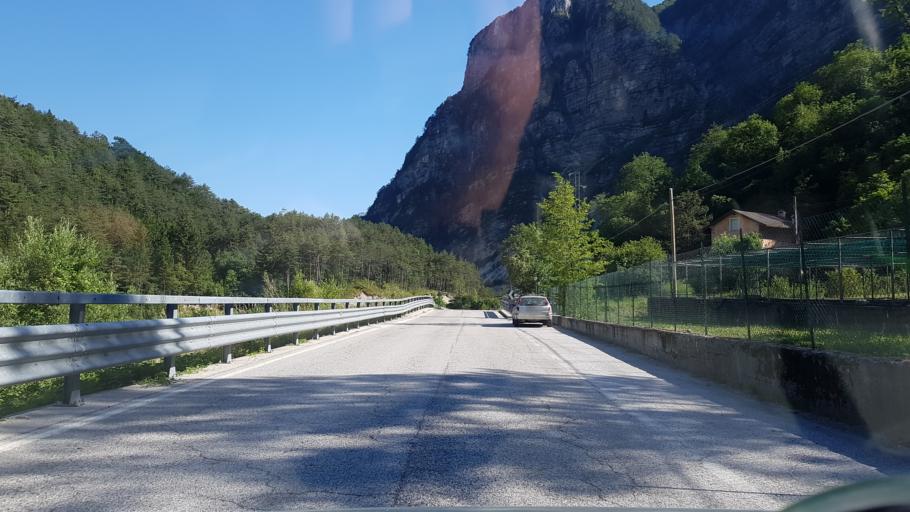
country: IT
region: Friuli Venezia Giulia
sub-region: Provincia di Udine
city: Moggio Udinese
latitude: 46.4503
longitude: 13.1876
